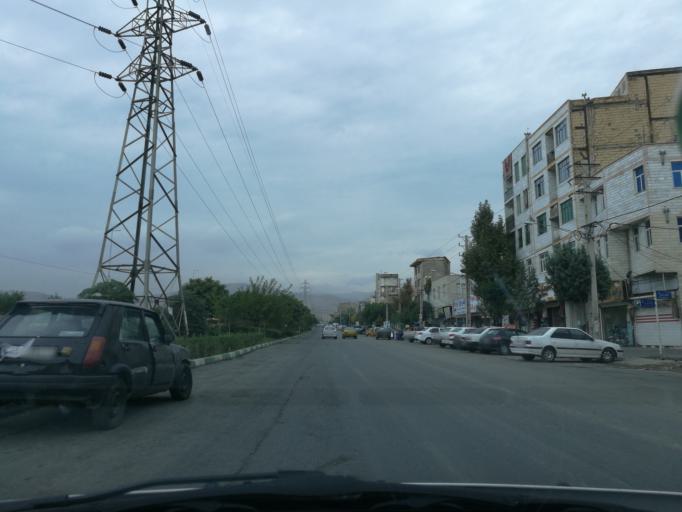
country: IR
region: Alborz
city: Karaj
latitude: 35.8494
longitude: 50.9169
